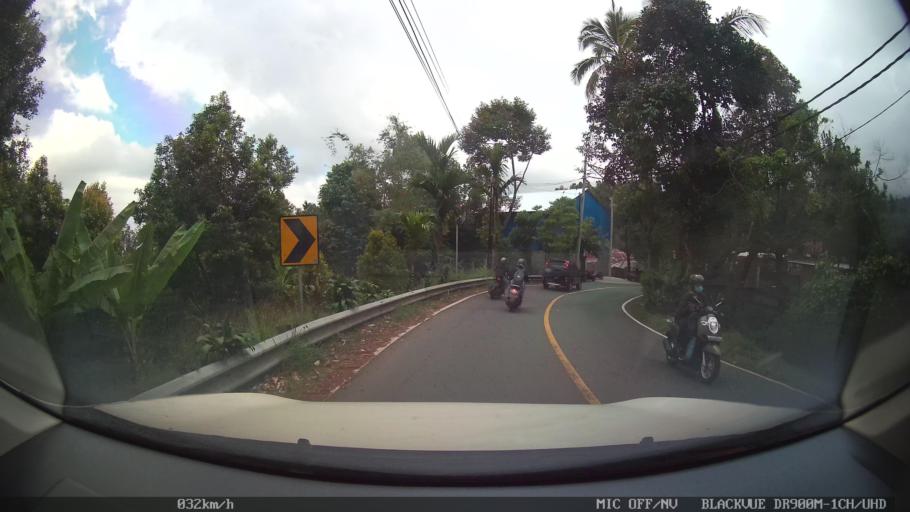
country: ID
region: Bali
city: Banjar Ambengan
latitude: -8.1968
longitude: 115.1396
